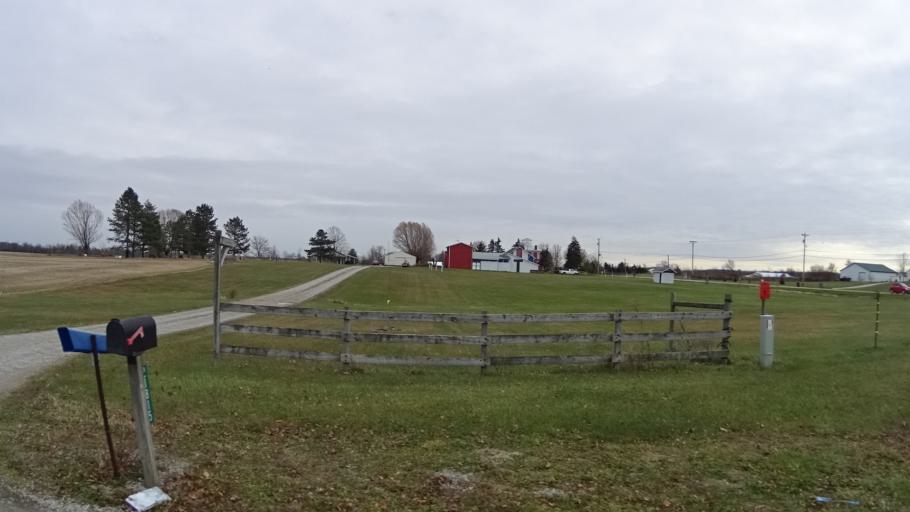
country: US
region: Ohio
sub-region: Lorain County
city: Wellington
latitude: 41.1689
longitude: -82.1934
